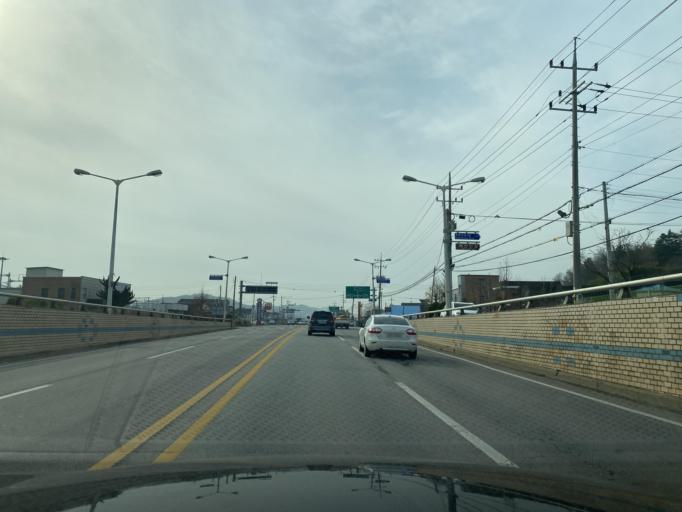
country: KR
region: Chungcheongnam-do
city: Yesan
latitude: 36.6931
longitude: 126.8281
